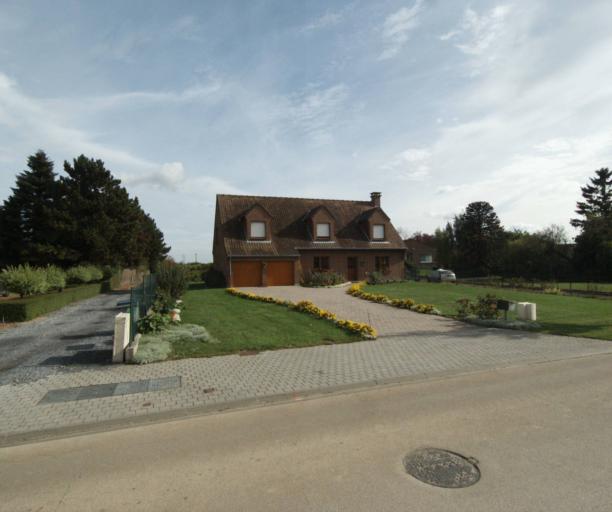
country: FR
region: Nord-Pas-de-Calais
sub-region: Departement du Nord
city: Radinghem-en-Weppes
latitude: 50.6257
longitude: 2.9036
